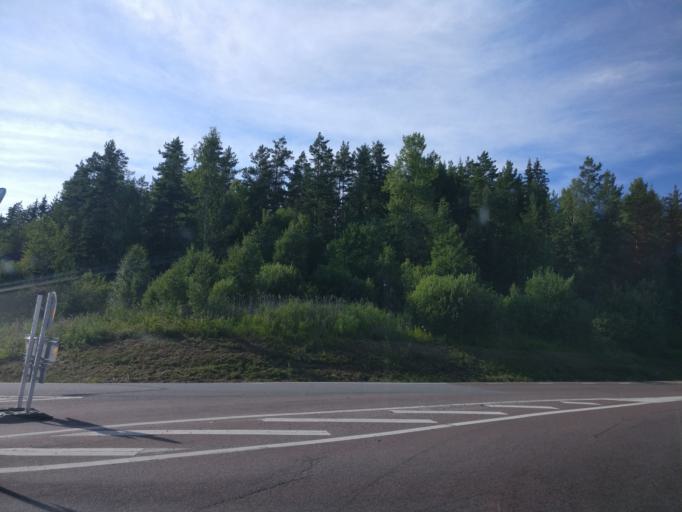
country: SE
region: Vaermland
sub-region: Arvika Kommun
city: Arvika
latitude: 59.6621
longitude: 12.6240
